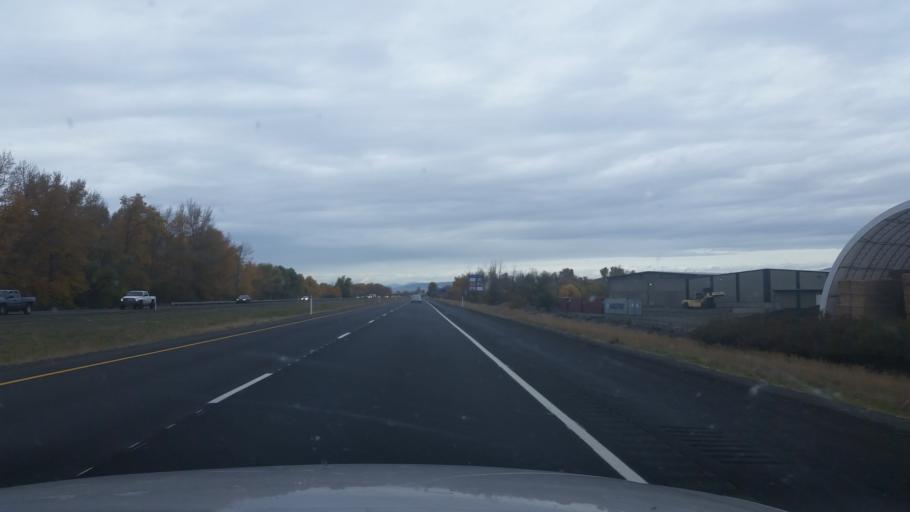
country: US
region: Washington
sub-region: Kittitas County
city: Ellensburg
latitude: 46.9946
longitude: -120.5767
